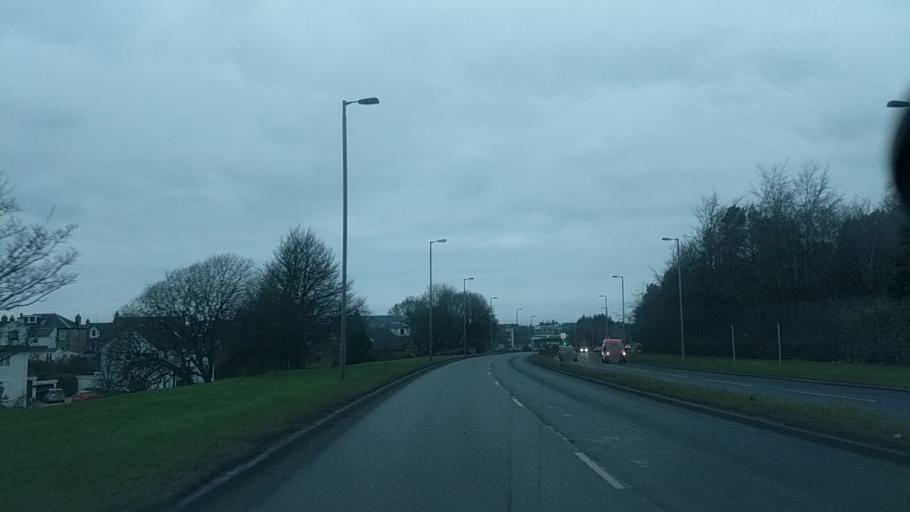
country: GB
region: Scotland
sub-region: South Lanarkshire
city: East Kilbride
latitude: 55.7649
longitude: -4.1663
